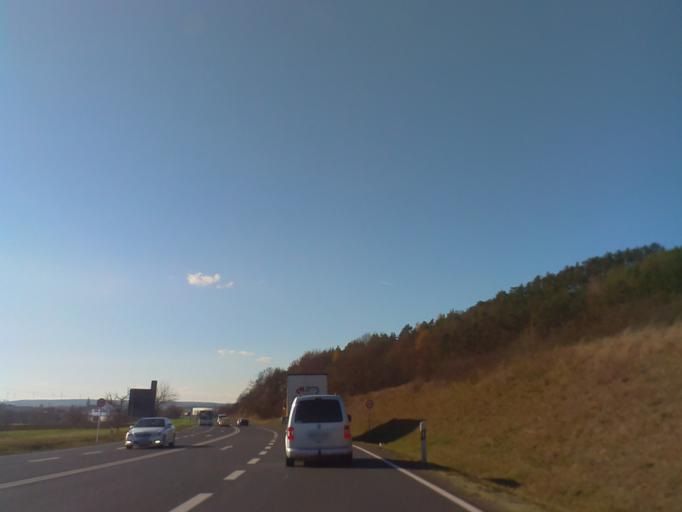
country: DE
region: Bavaria
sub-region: Regierungsbezirk Unterfranken
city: Heustreu
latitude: 50.3407
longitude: 10.2400
